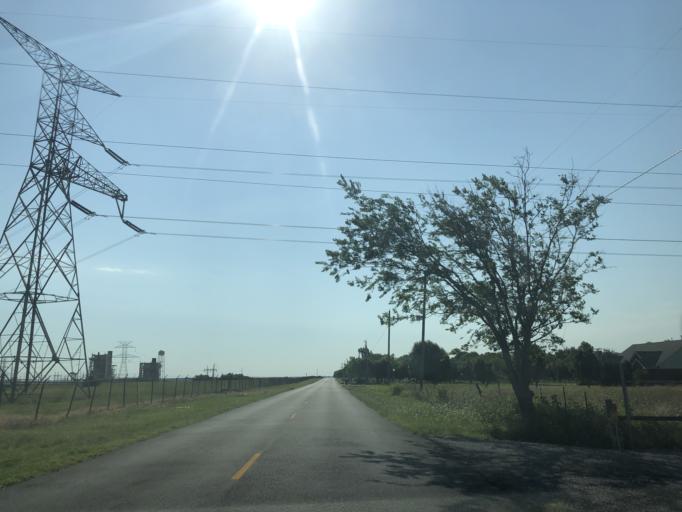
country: US
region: Texas
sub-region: Dallas County
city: Sunnyvale
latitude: 32.8337
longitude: -96.5561
